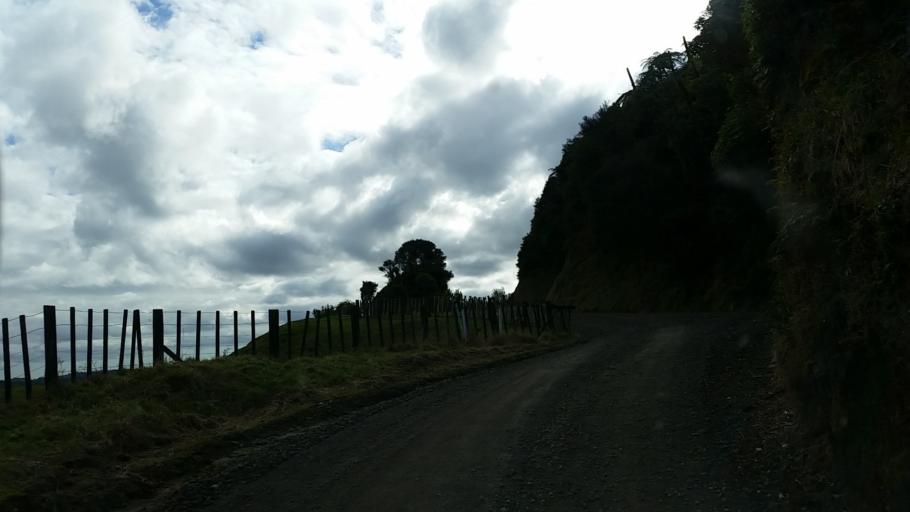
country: NZ
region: Taranaki
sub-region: South Taranaki District
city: Eltham
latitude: -39.1729
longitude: 174.6192
